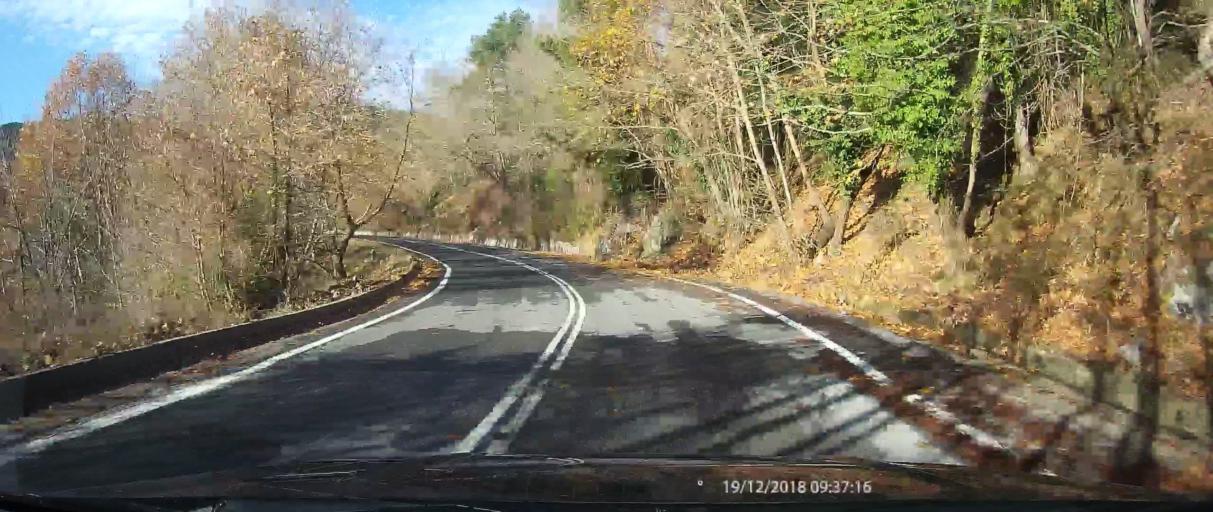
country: GR
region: Peloponnese
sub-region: Nomos Lakonias
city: Magoula
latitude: 37.0813
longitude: 22.2799
